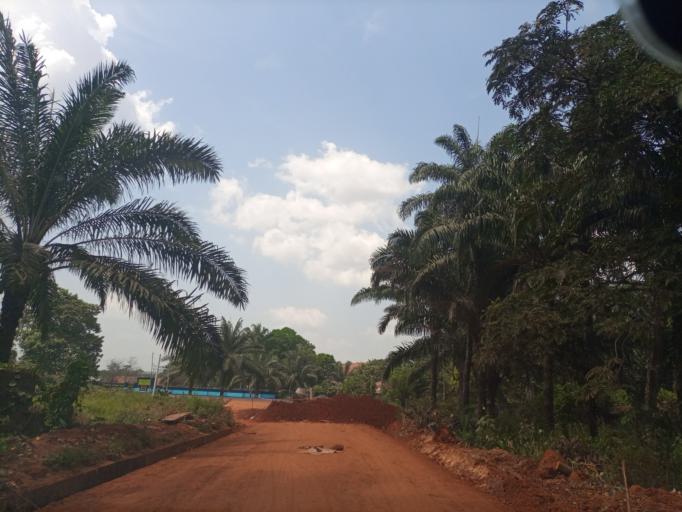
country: NG
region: Enugu
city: Obollo-Afor
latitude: 6.8695
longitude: 7.4708
